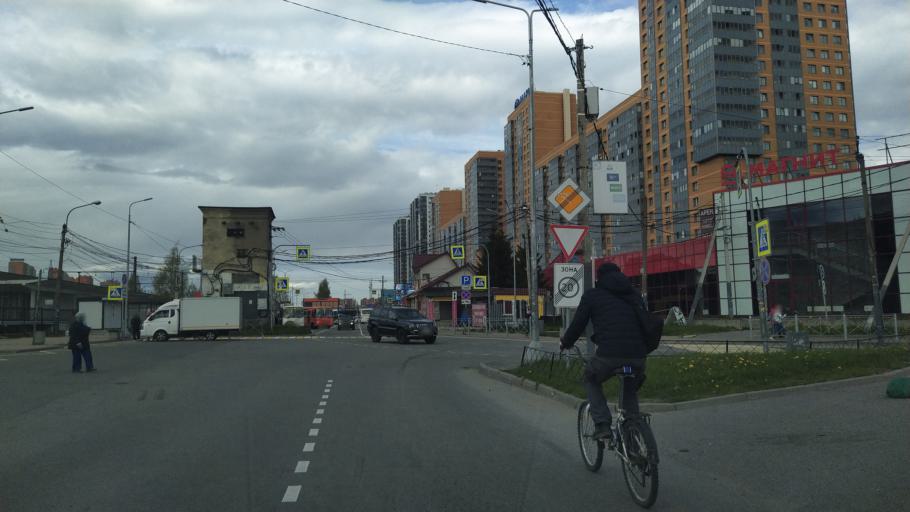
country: RU
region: Leningrad
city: Murino
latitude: 60.0489
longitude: 30.4429
